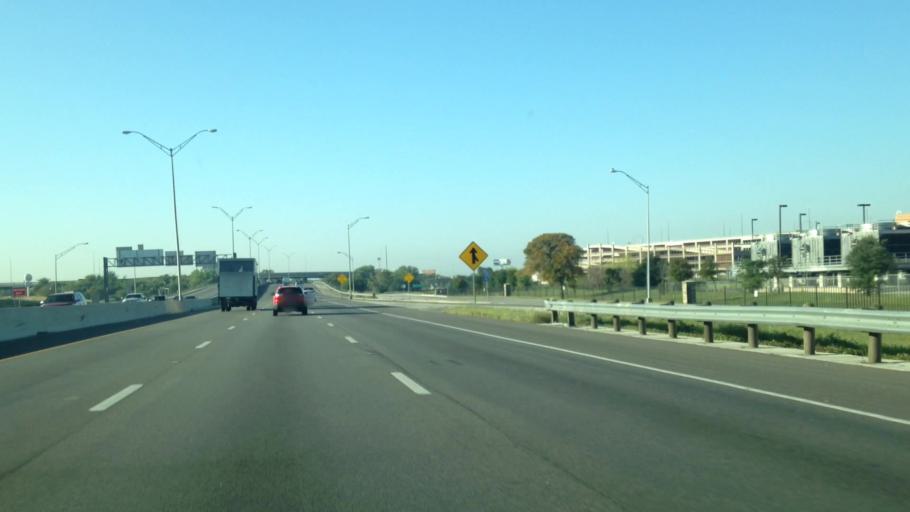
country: US
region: Texas
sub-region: Bexar County
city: Kirby
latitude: 29.4600
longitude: -98.4115
